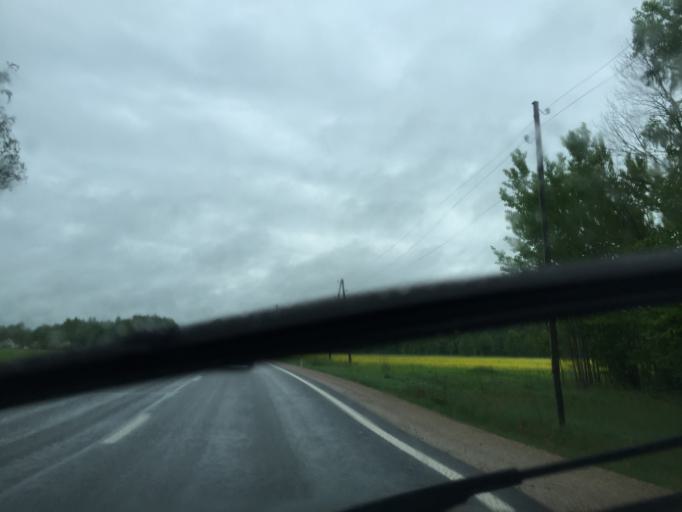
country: LV
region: Ogre
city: Jumprava
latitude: 56.6868
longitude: 24.8969
